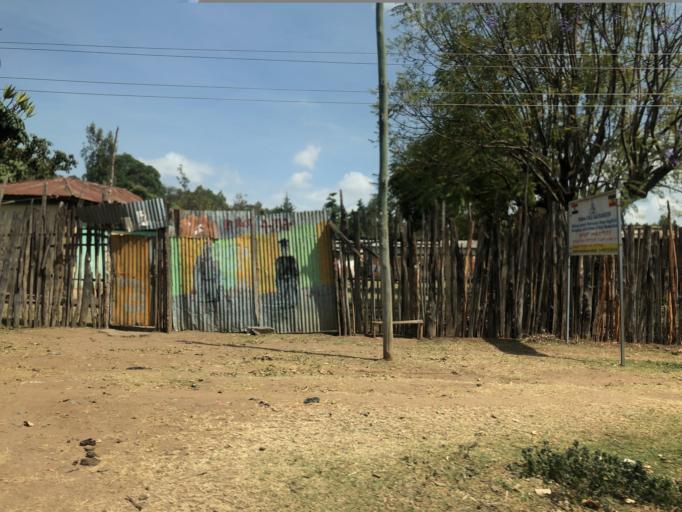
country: ET
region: Oromiya
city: Shashemene
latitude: 7.2729
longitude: 38.6551
